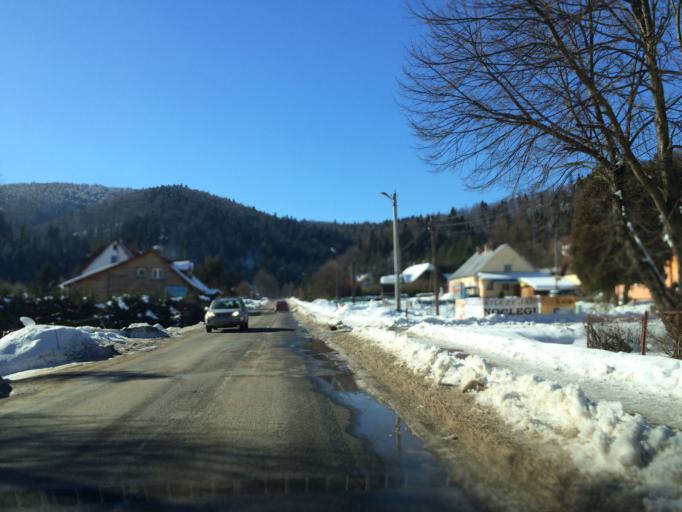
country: PL
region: Subcarpathian Voivodeship
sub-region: Powiat leski
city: Cisna
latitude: 49.2101
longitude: 22.3278
